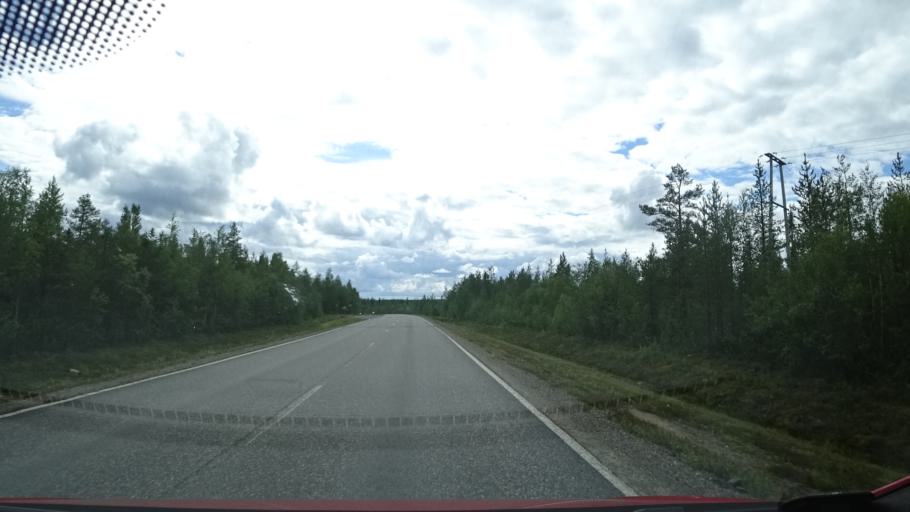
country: FI
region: Lapland
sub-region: Tunturi-Lappi
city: Kittilae
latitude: 67.5383
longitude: 24.9089
